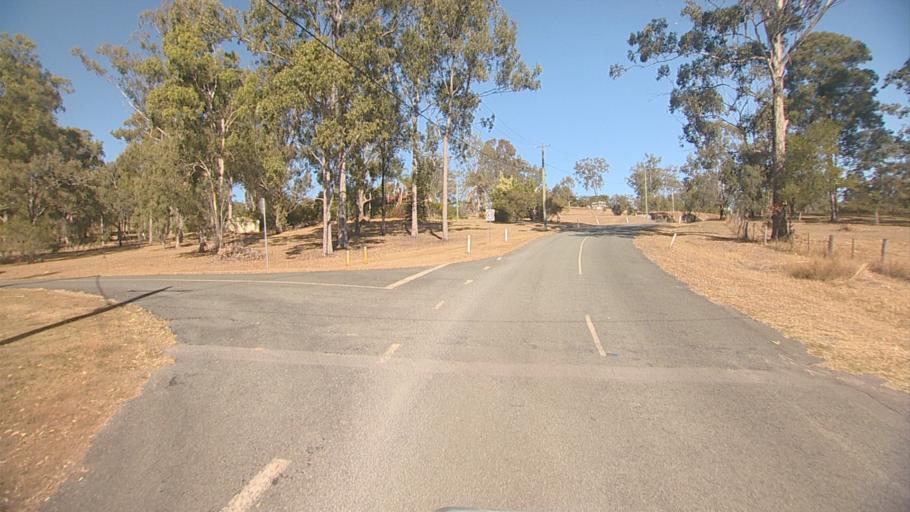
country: AU
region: Queensland
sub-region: Logan
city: Cedar Vale
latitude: -27.8859
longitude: 152.9998
